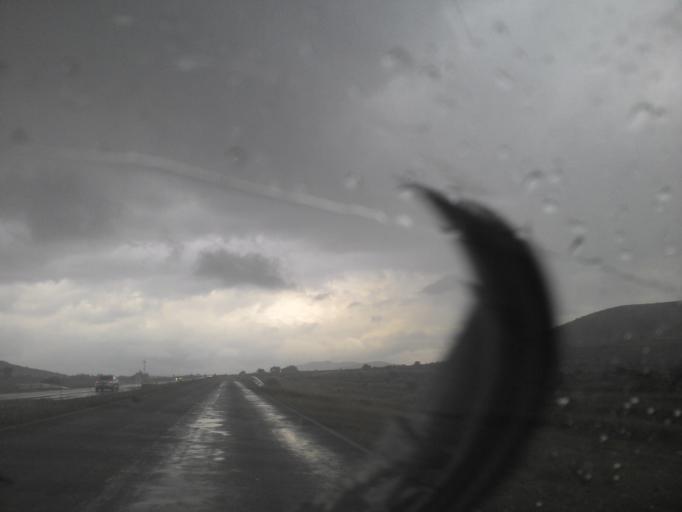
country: MX
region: Hidalgo
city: Zempoala
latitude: 19.8946
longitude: -98.6156
